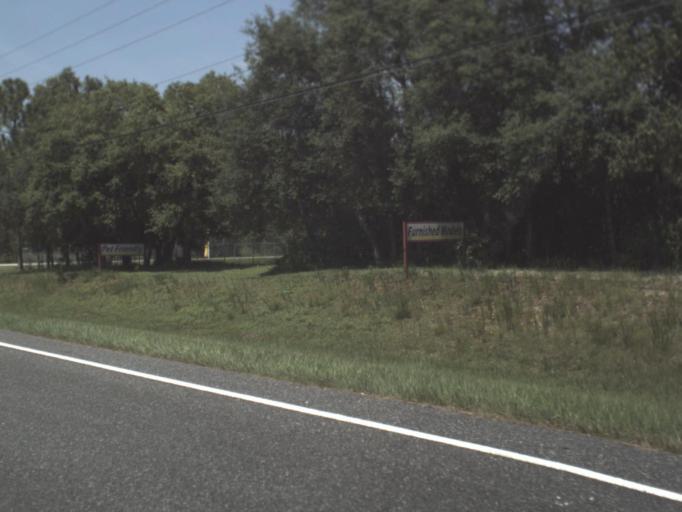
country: US
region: Florida
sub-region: Citrus County
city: Sugarmill Woods
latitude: 28.7080
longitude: -82.5525
